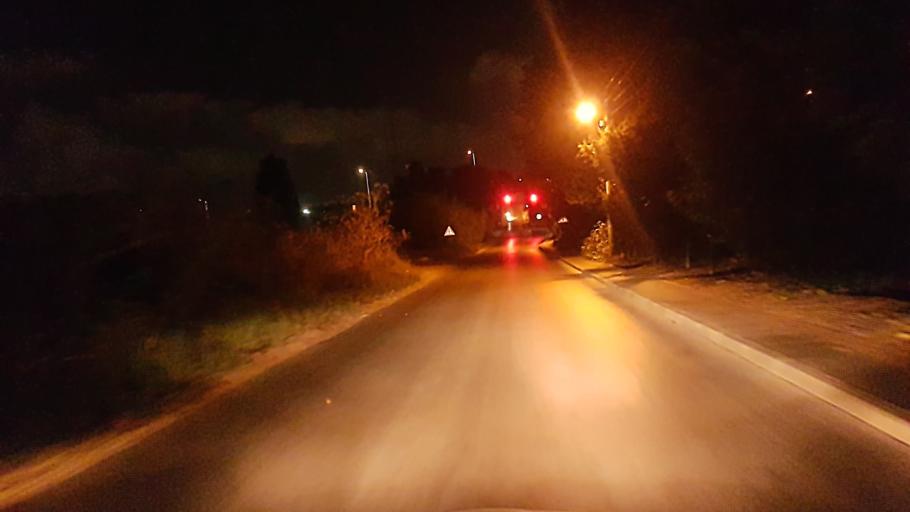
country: IL
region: Central District
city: Hod HaSharon
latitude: 32.1625
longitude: 34.8799
